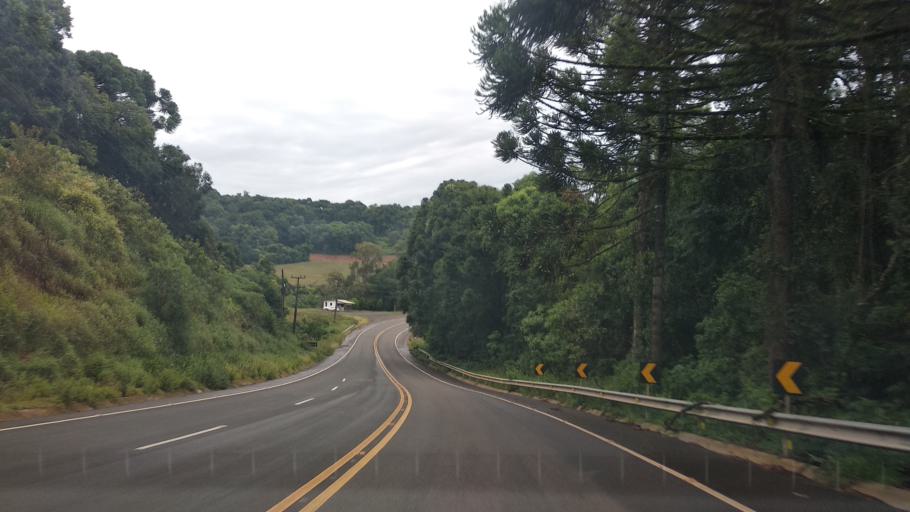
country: BR
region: Santa Catarina
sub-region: Videira
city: Videira
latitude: -27.0463
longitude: -51.1565
